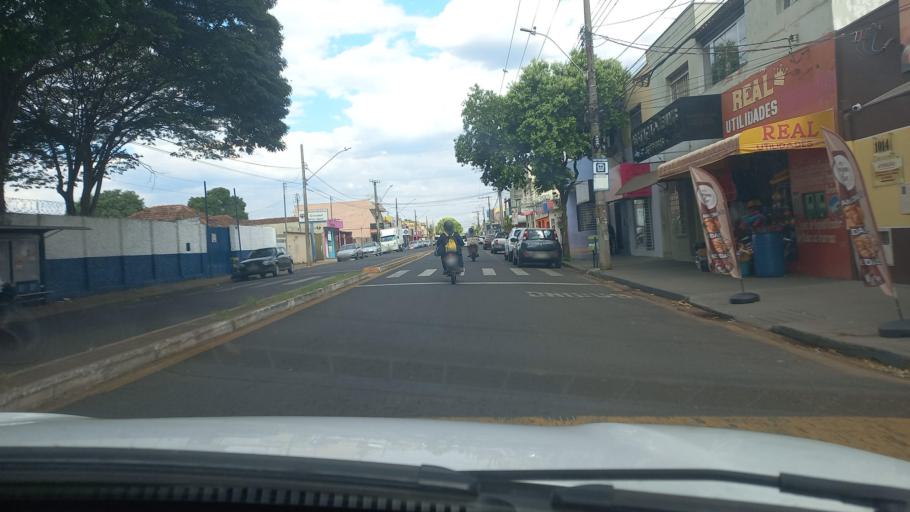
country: BR
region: Minas Gerais
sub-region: Uberaba
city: Uberaba
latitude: -19.7345
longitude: -47.9200
